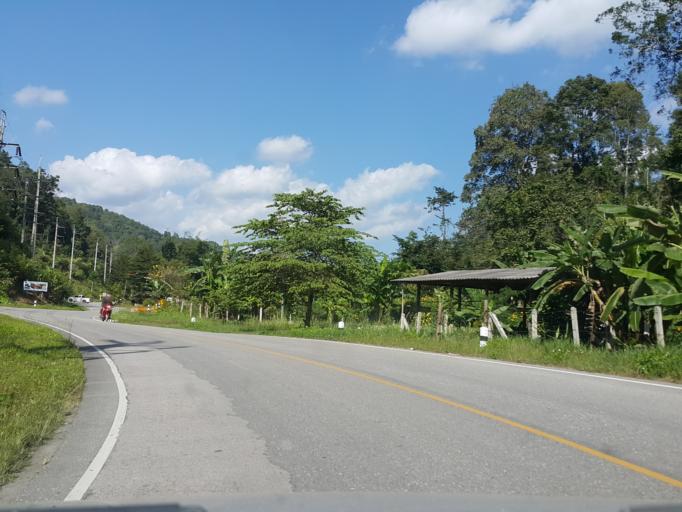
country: TH
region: Chiang Mai
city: Mae Taeng
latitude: 19.1582
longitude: 98.6917
